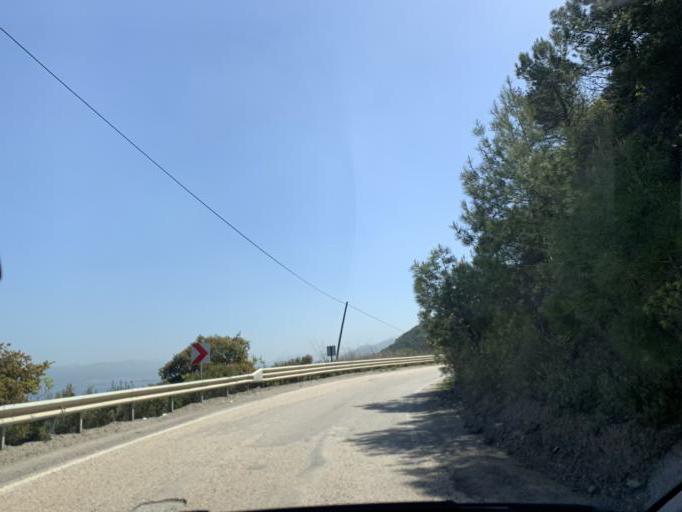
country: TR
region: Bursa
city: Niluefer
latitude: 40.3560
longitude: 28.9824
